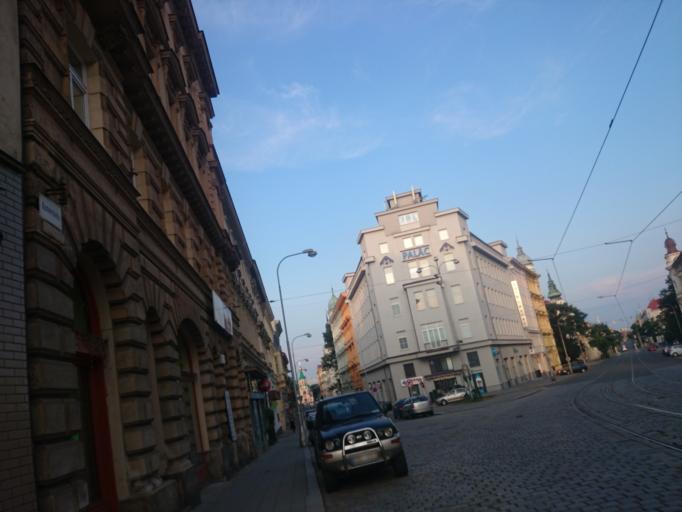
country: CZ
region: Olomoucky
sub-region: Okres Olomouc
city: Olomouc
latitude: 49.5969
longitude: 17.2620
